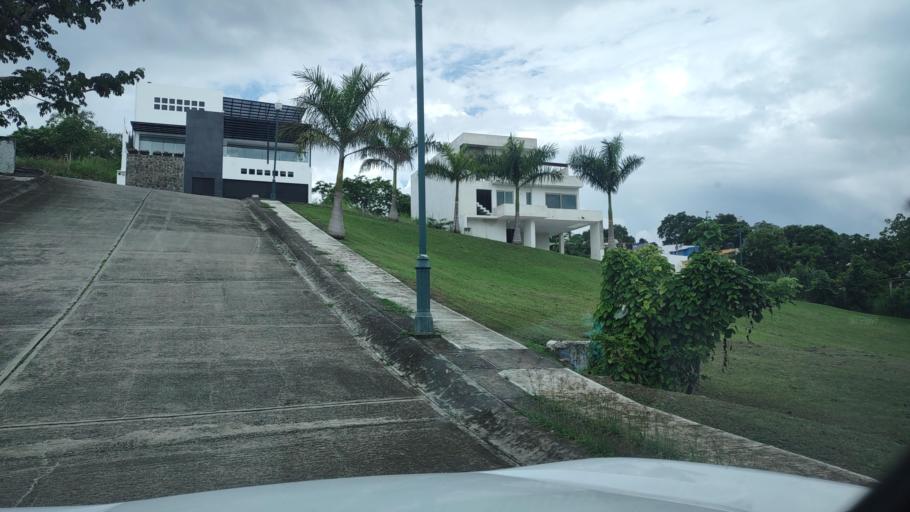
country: MX
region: Veracruz
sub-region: Tuxpan
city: Alto Lucero
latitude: 20.9445
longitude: -97.4262
